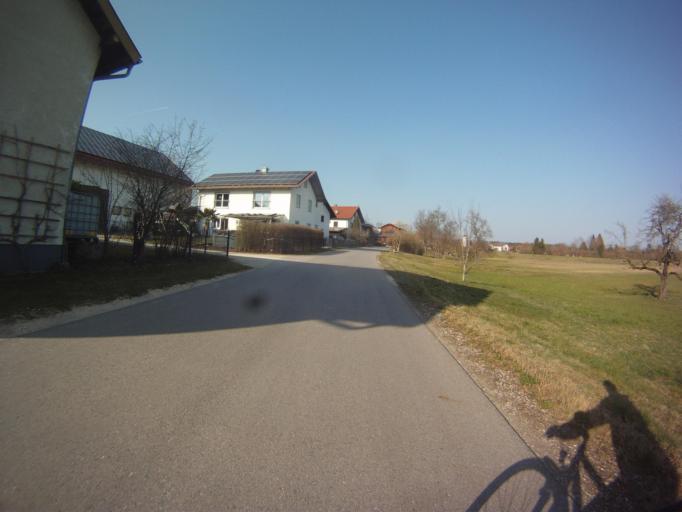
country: DE
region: Bavaria
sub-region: Upper Bavaria
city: Haiming
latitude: 48.2232
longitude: 12.8758
